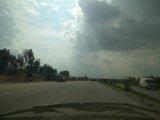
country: IN
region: Karnataka
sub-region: Bangalore Rural
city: Dasarahalli
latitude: 13.1308
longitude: 77.9573
